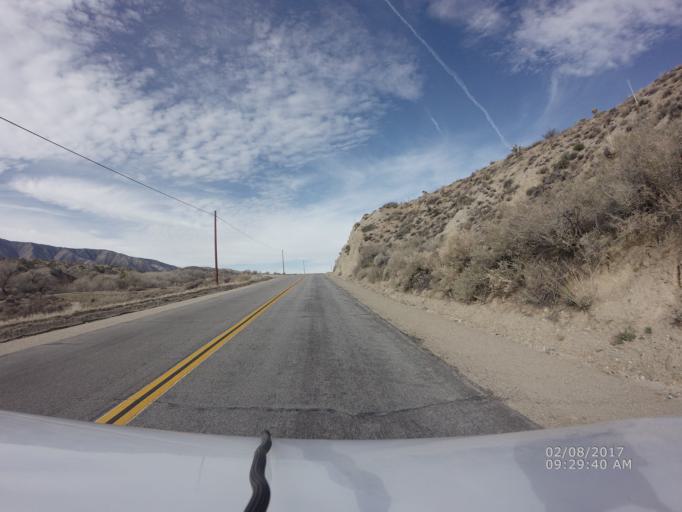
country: US
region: California
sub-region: Los Angeles County
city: Littlerock
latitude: 34.4566
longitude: -117.8865
